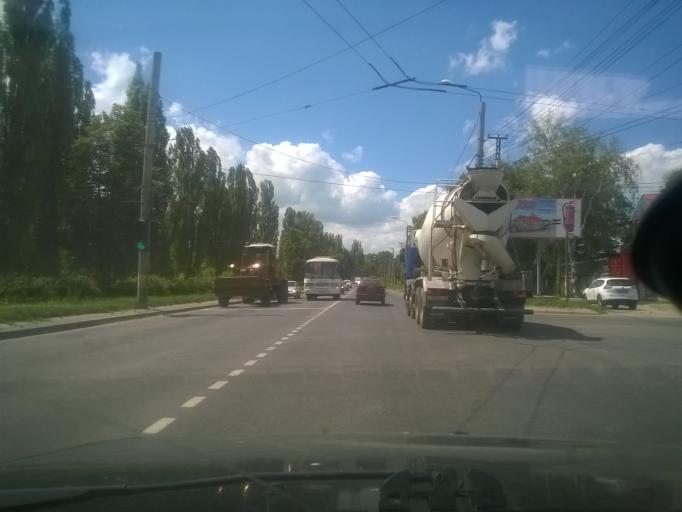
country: RU
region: Kursk
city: Kursk
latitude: 51.6621
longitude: 36.1314
